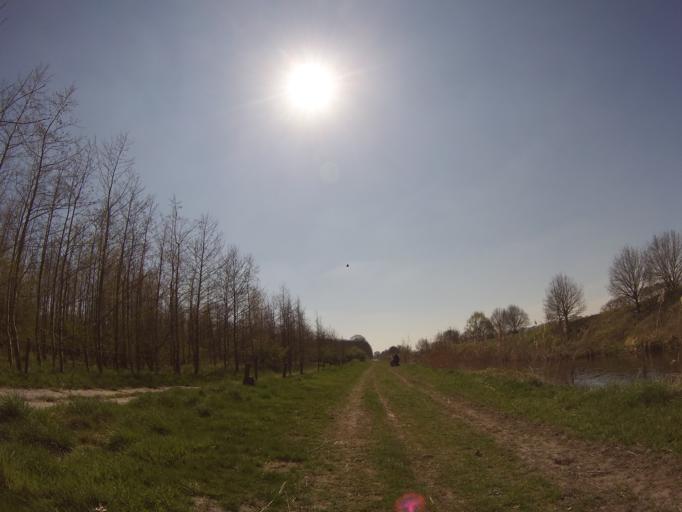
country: NL
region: Utrecht
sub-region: Gemeente Utrechtse Heuvelrug
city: Overberg
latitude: 52.0644
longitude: 5.4791
